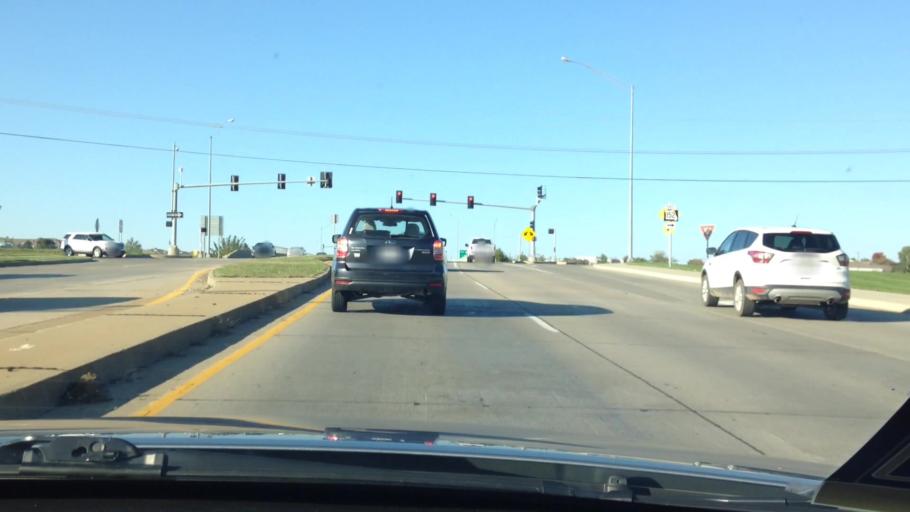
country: US
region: Missouri
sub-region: Clay County
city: Gladstone
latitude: 39.2592
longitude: -94.5757
